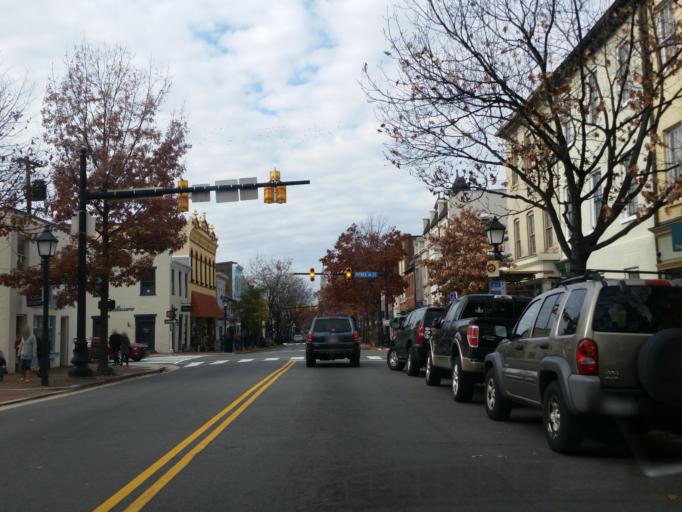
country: US
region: Virginia
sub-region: City of Alexandria
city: Alexandria
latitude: 38.8054
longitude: -77.0497
